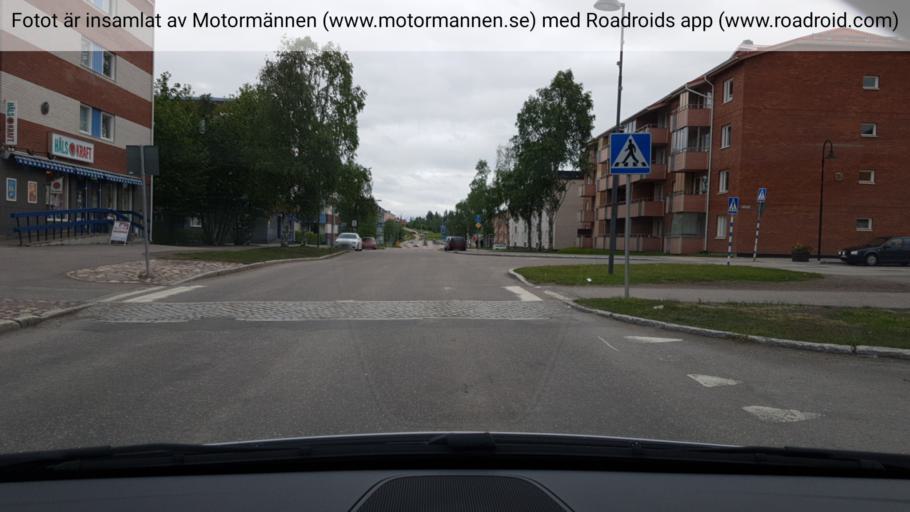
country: SE
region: Norrbotten
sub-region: Gallivare Kommun
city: Gaellivare
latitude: 67.1355
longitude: 20.6547
